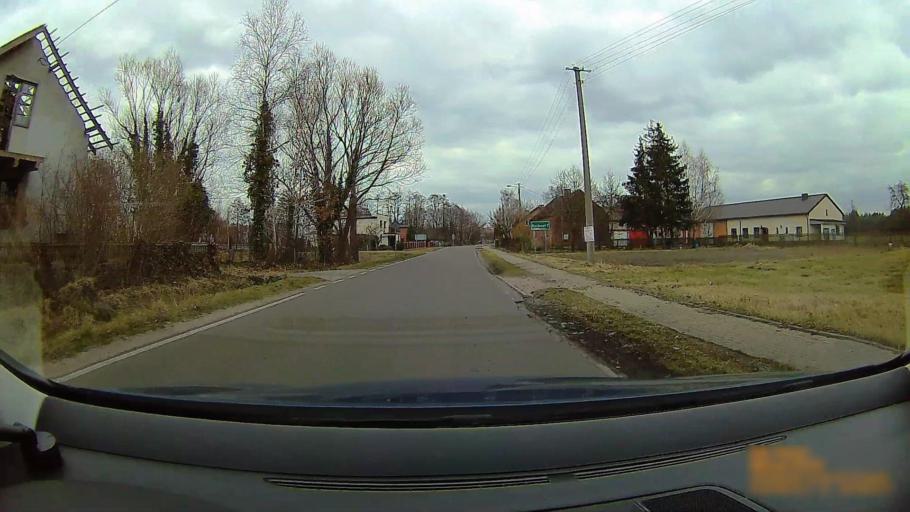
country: PL
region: Greater Poland Voivodeship
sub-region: Powiat koninski
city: Rzgow Pierwszy
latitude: 52.1039
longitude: 18.0910
